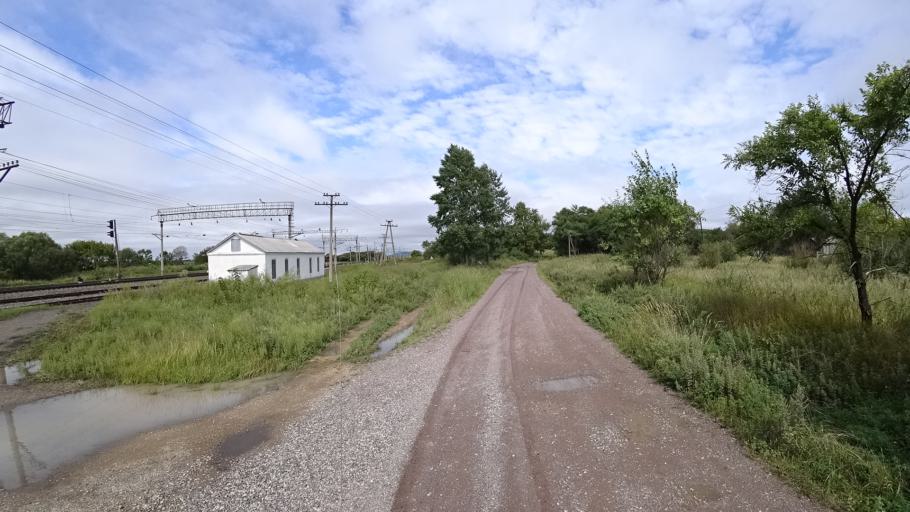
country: RU
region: Primorskiy
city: Lyalichi
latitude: 44.1377
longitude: 132.3735
